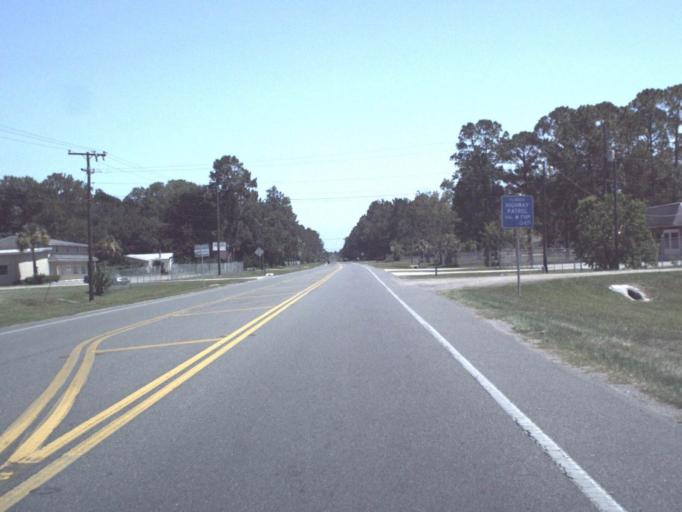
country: US
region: Florida
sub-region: Baker County
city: Macclenny
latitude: 30.3003
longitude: -82.1259
